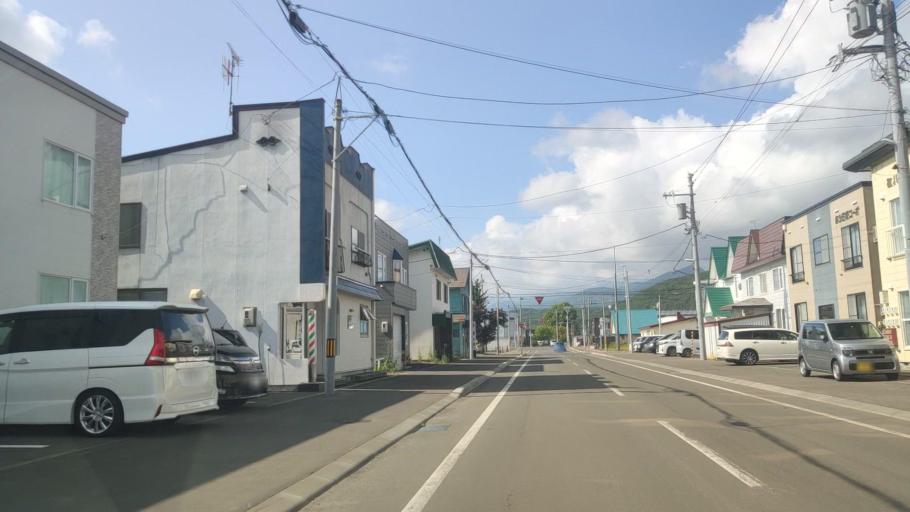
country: JP
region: Hokkaido
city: Shimo-furano
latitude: 43.3439
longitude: 142.3860
